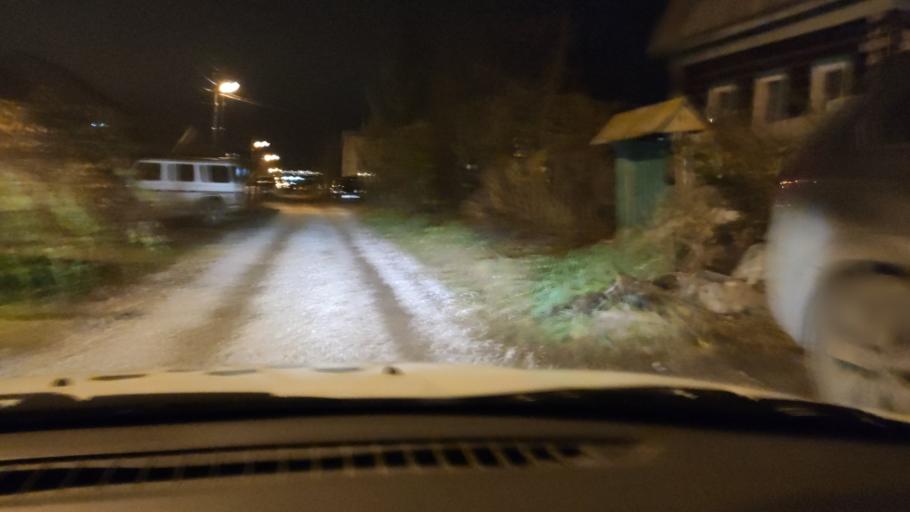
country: RU
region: Perm
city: Kondratovo
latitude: 58.0490
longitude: 56.1182
